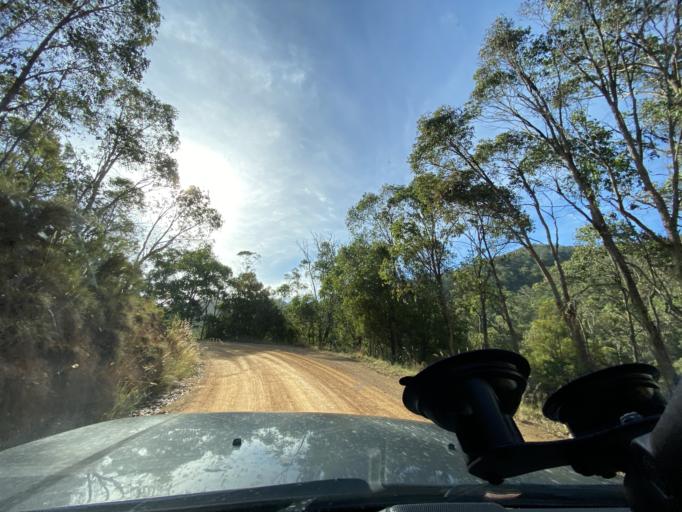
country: AU
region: Victoria
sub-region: Mansfield
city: Mansfield
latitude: -37.5172
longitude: 146.0877
